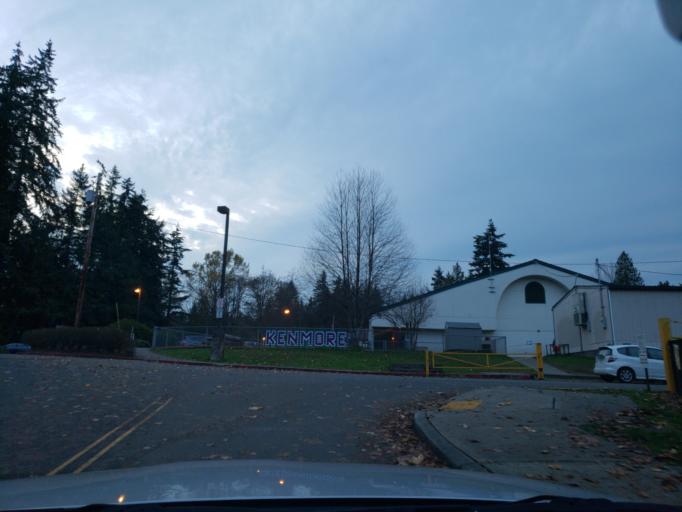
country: US
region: Washington
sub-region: King County
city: Kenmore
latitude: 47.7674
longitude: -122.2449
